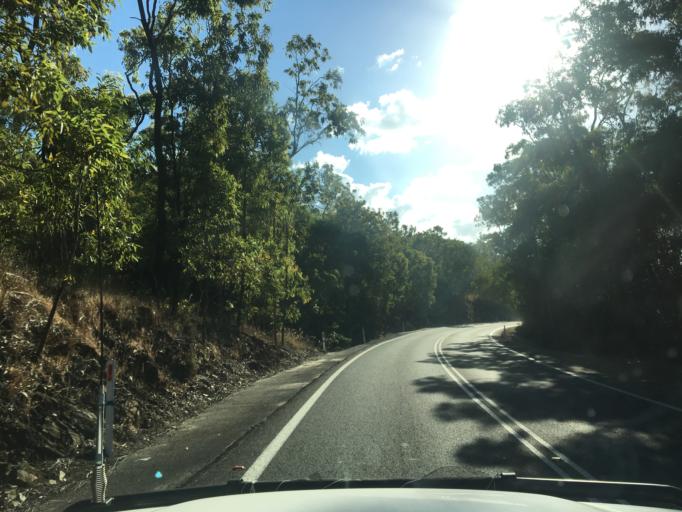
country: AU
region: Queensland
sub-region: Cairns
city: Palm Cove
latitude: -16.6996
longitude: 145.6172
